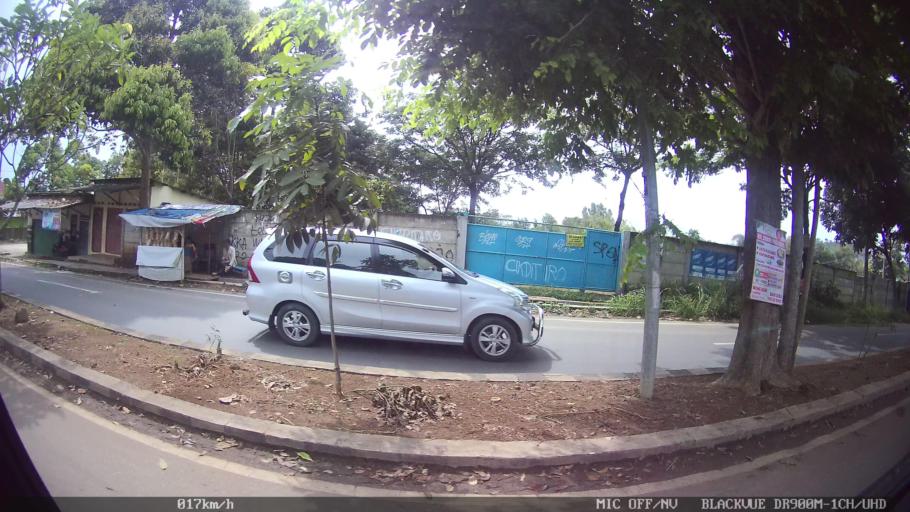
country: ID
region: Lampung
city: Bandarlampung
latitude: -5.4052
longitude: 105.2001
